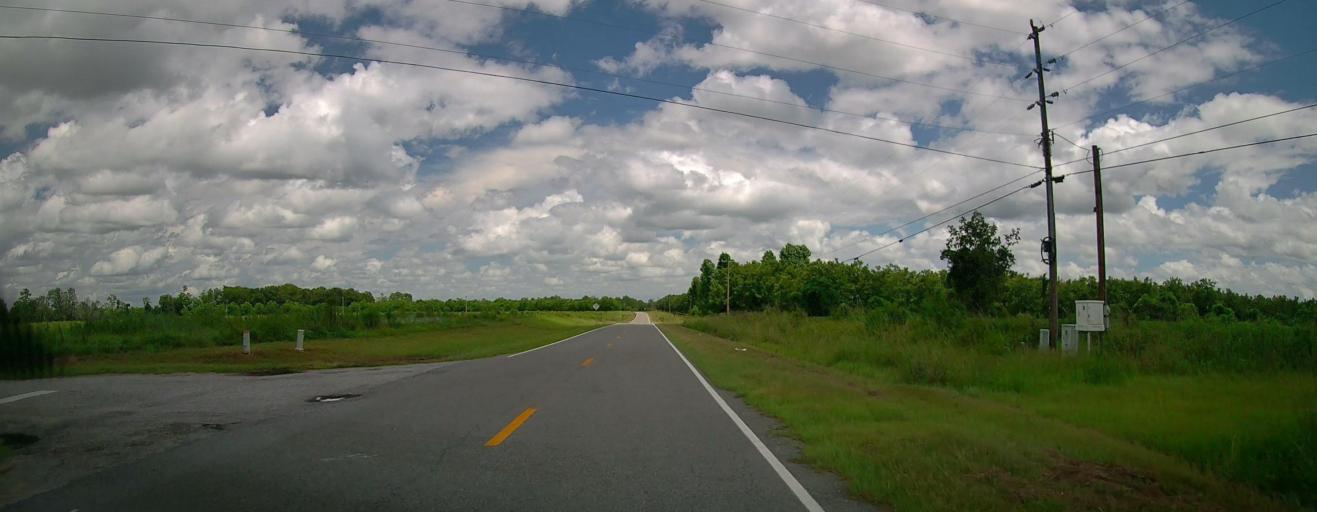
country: US
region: Georgia
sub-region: Irwin County
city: Ocilla
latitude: 31.6460
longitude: -83.2865
